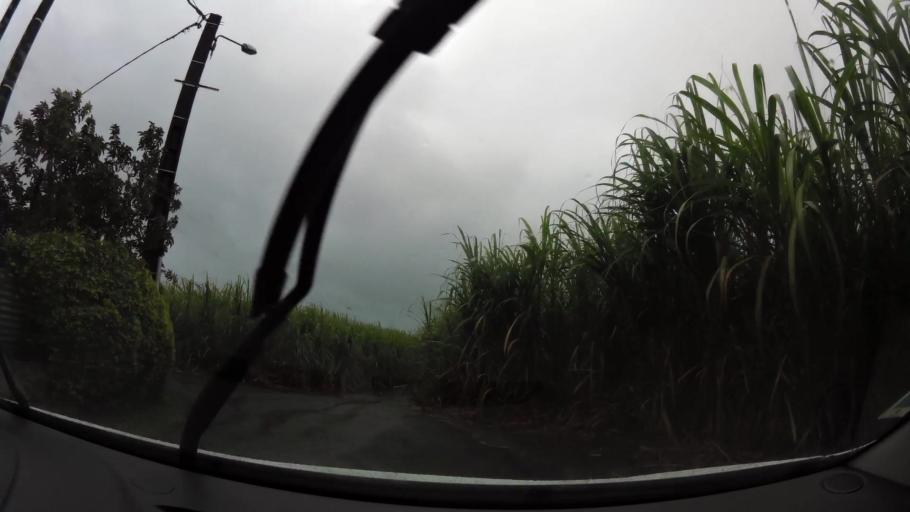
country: RE
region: Reunion
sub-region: Reunion
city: Saint-Benoit
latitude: -21.0216
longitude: 55.6964
